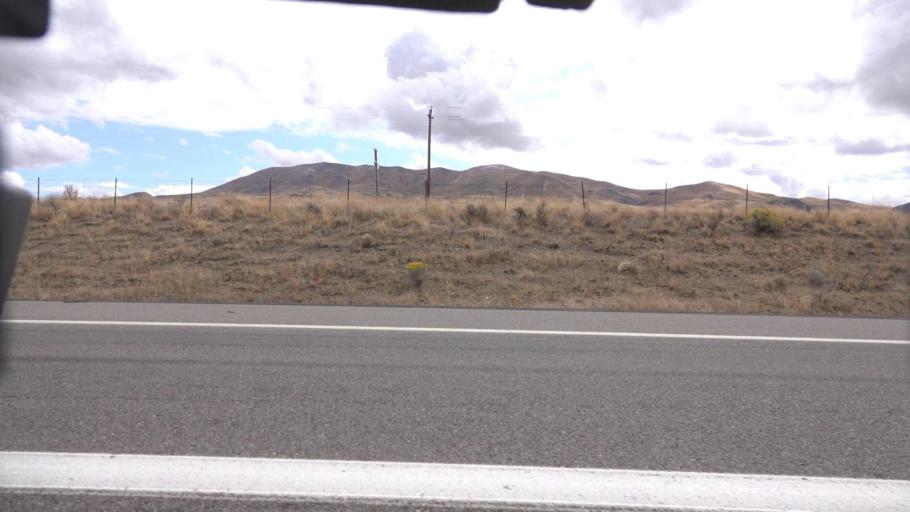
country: US
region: Nevada
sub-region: Elko County
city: Elko
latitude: 40.9314
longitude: -115.6690
